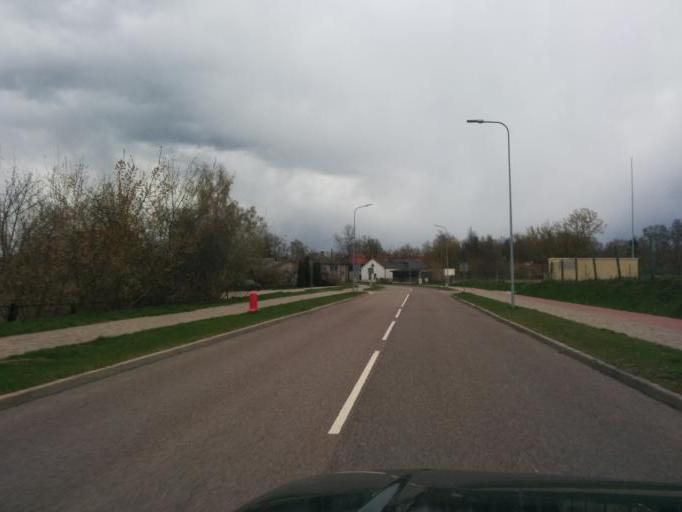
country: LV
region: Jelgava
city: Jelgava
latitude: 56.6522
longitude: 23.7436
